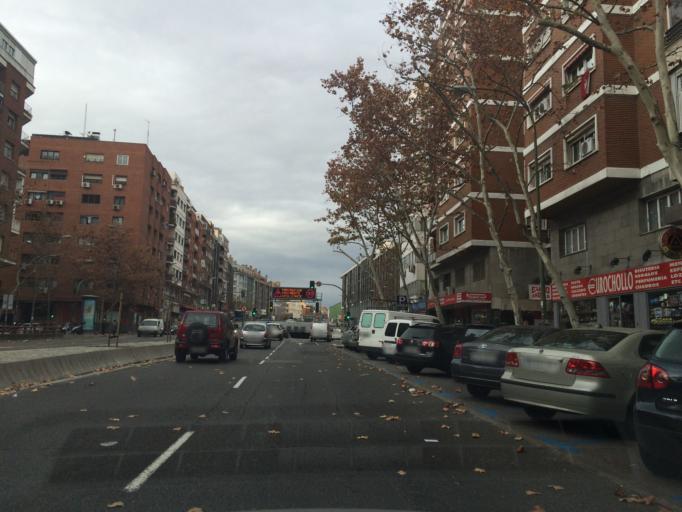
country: ES
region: Madrid
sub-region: Provincia de Madrid
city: Chamartin
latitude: 40.4598
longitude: -3.6957
